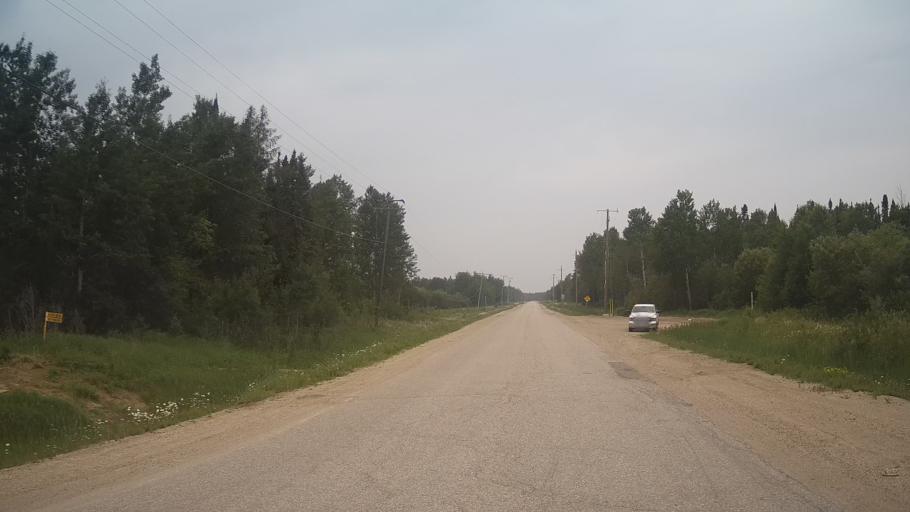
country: CA
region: Ontario
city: Hearst
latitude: 49.7450
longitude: -84.1268
